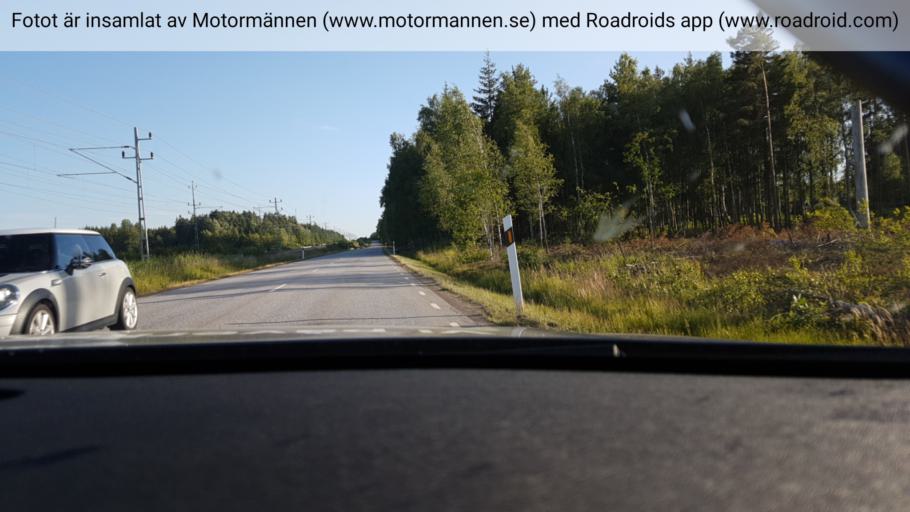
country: SE
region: Vaestra Goetaland
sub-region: Toreboda Kommun
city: Toereboda
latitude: 58.6761
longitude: 14.1009
